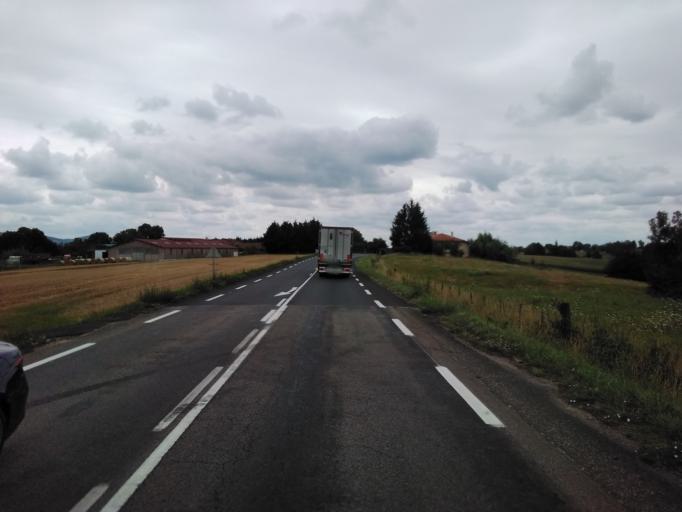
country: FR
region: Rhone-Alpes
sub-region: Departement de l'Ain
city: Coligny
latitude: 46.3572
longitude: 5.3291
